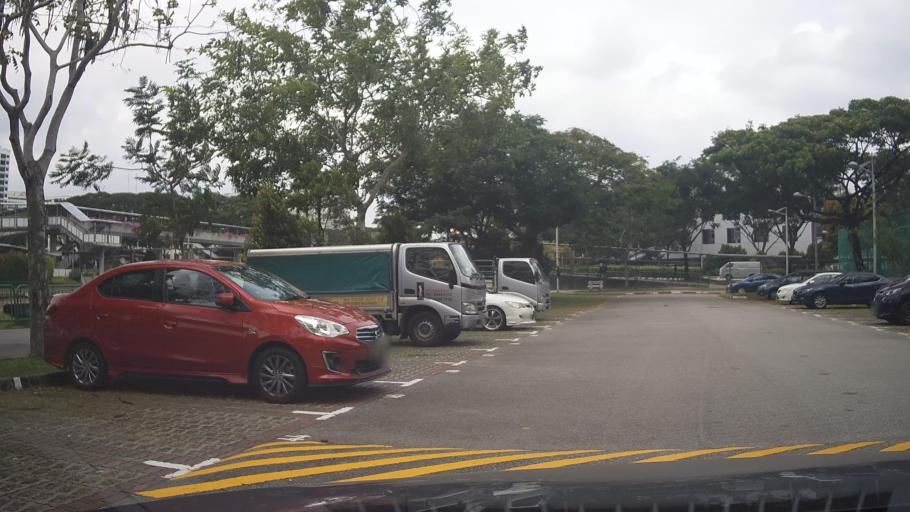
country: SG
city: Singapore
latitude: 1.3037
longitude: 103.8834
